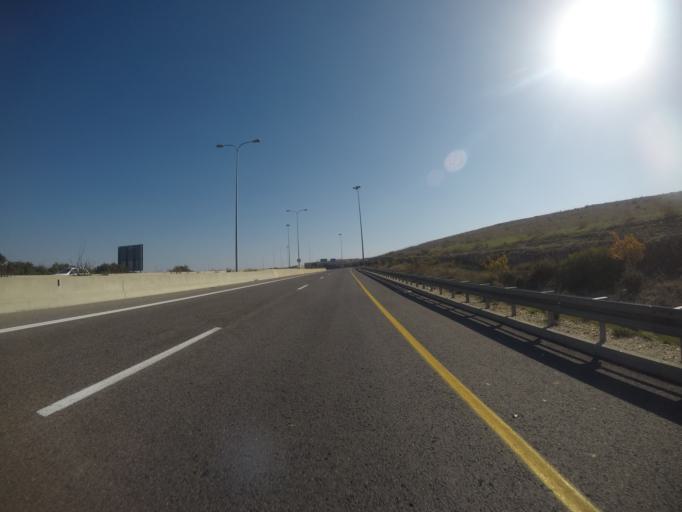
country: IL
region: Haifa
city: Daliyat el Karmil
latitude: 32.6103
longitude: 35.0393
